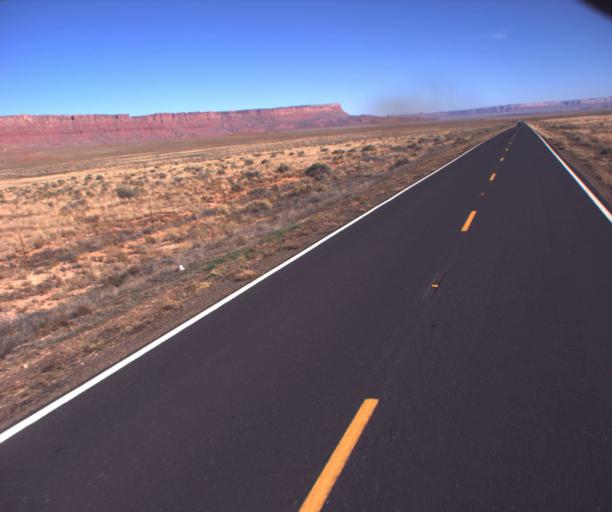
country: US
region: Arizona
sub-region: Coconino County
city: Fredonia
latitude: 36.7218
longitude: -112.0155
